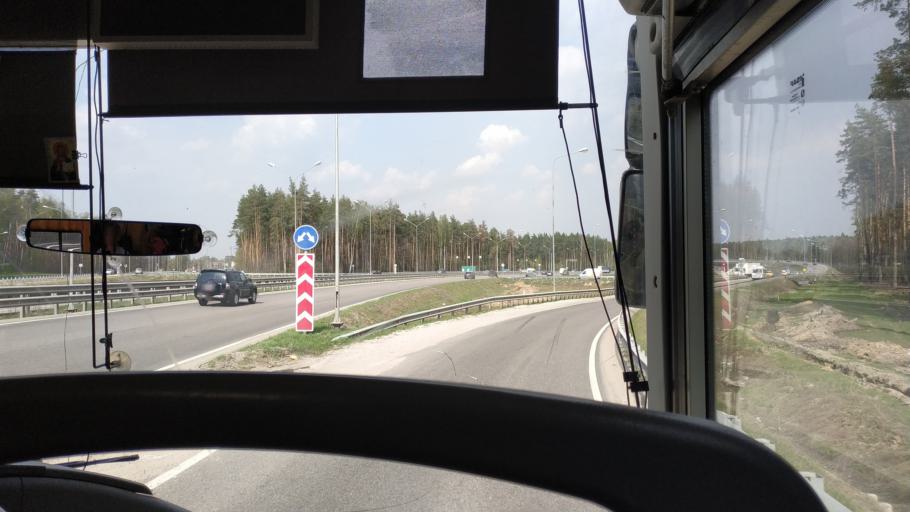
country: RU
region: Moskovskaya
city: Lytkarino
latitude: 55.6167
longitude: 37.9223
